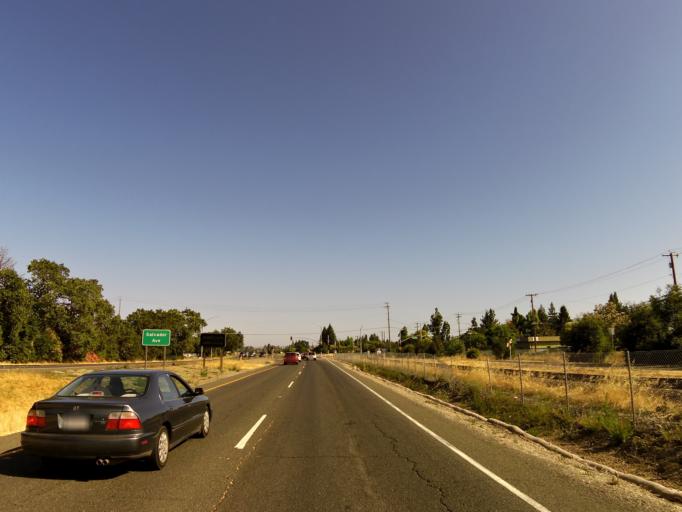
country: US
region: California
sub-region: Napa County
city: Napa
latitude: 38.3409
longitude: -122.3252
